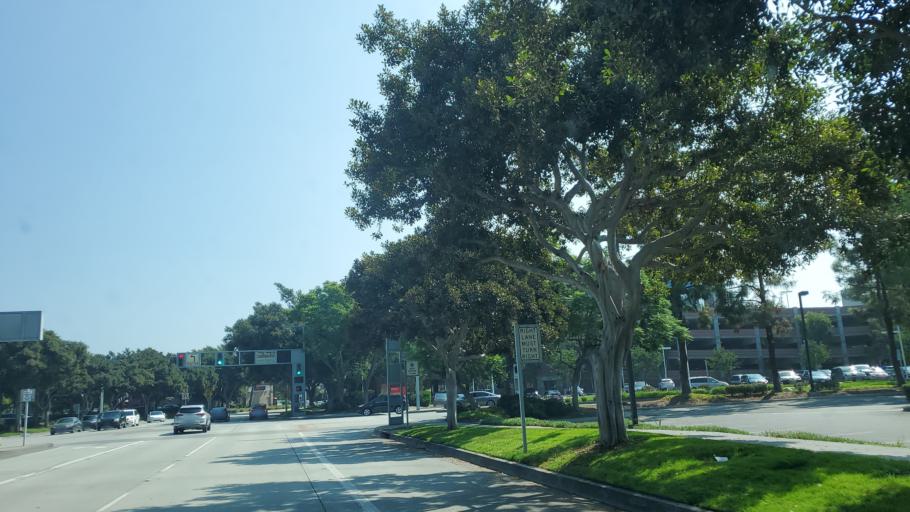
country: US
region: California
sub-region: Los Angeles County
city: Cerritos
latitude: 33.8703
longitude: -118.0631
